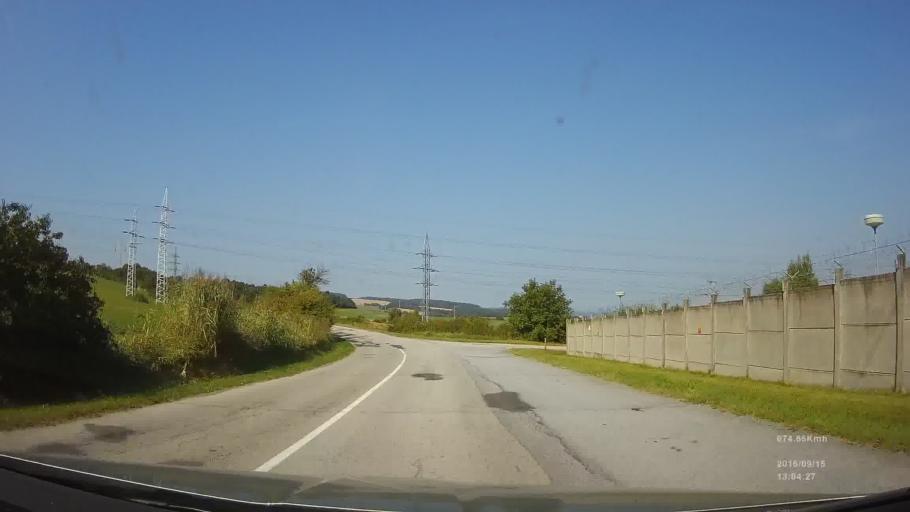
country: SK
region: Presovsky
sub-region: Okres Presov
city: Presov
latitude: 48.8583
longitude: 21.2521
